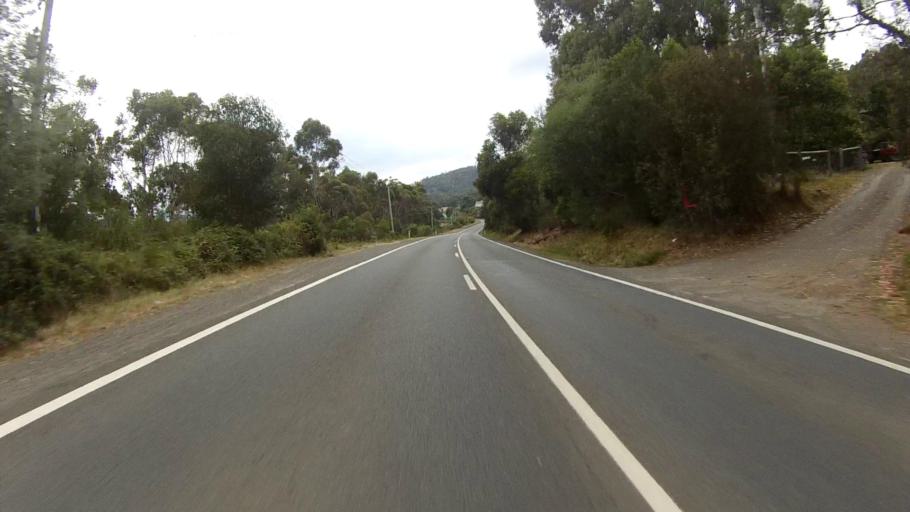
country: AU
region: Tasmania
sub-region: Huon Valley
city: Huonville
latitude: -43.0587
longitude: 147.0438
